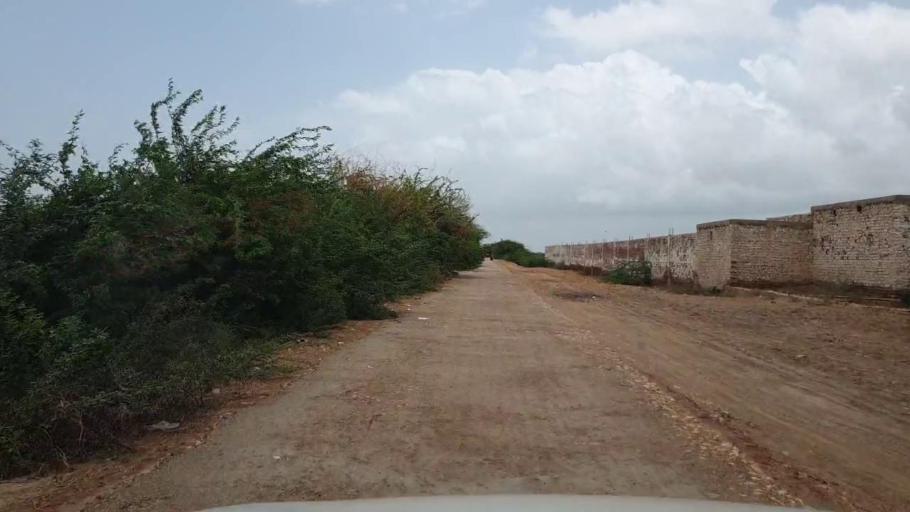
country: PK
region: Sindh
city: Kario
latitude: 24.6910
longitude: 68.6630
